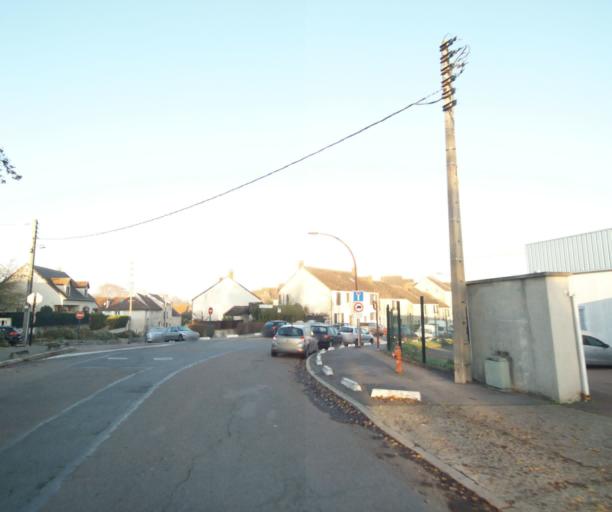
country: FR
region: Ile-de-France
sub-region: Departement du Val-d'Oise
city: Gonesse
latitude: 48.9830
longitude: 2.4527
